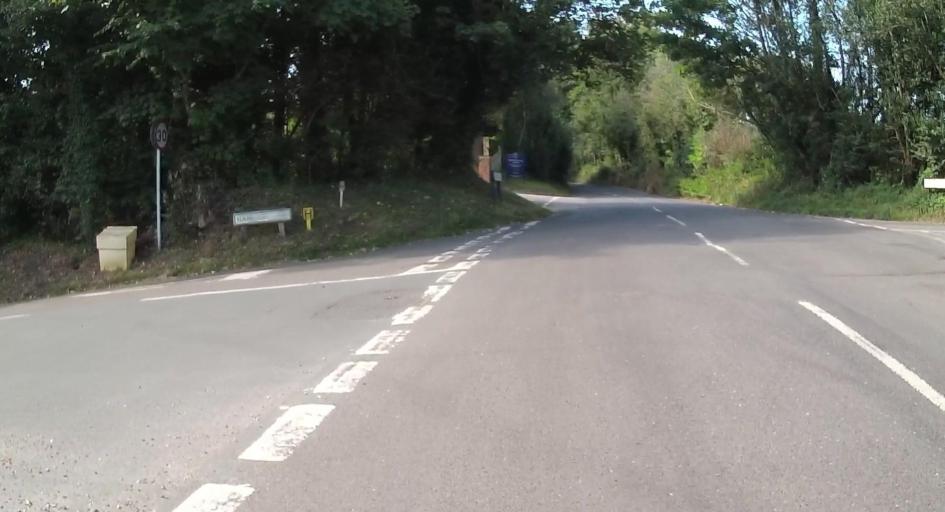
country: GB
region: England
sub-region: Surrey
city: Farnham
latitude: 51.1783
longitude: -0.7953
